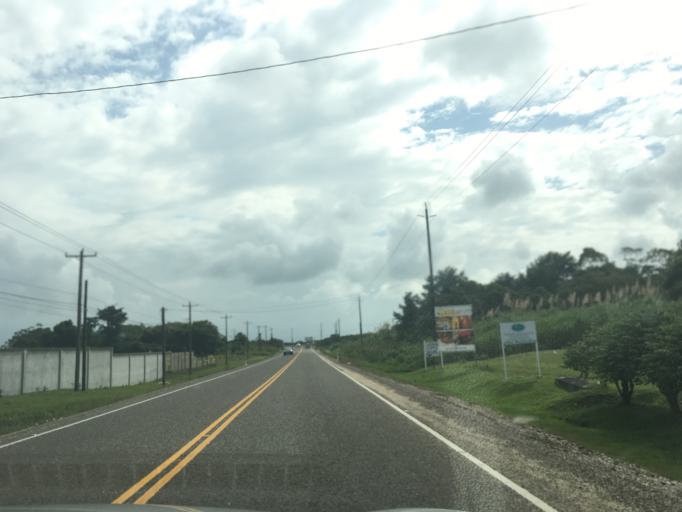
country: BZ
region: Stann Creek
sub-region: Dangriga
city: Dangriga
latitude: 16.9851
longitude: -88.2971
